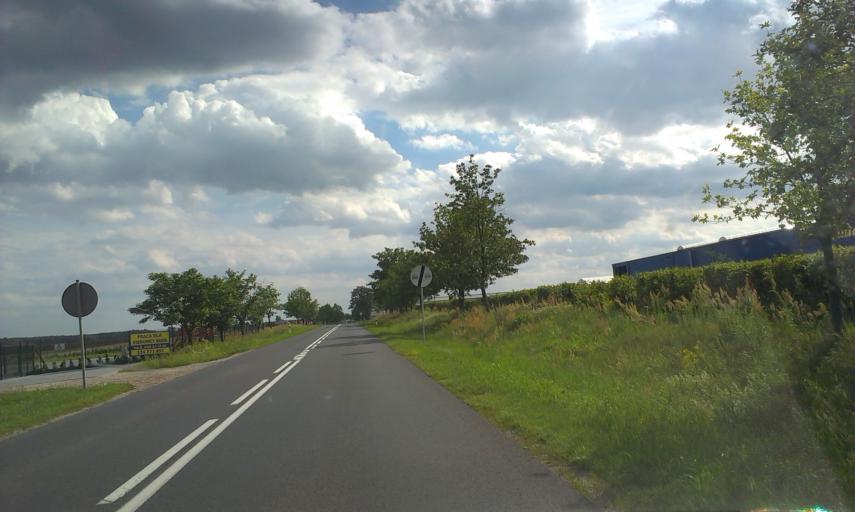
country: PL
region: Greater Poland Voivodeship
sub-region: Powiat zlotowski
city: Zlotow
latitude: 53.3431
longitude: 17.0163
